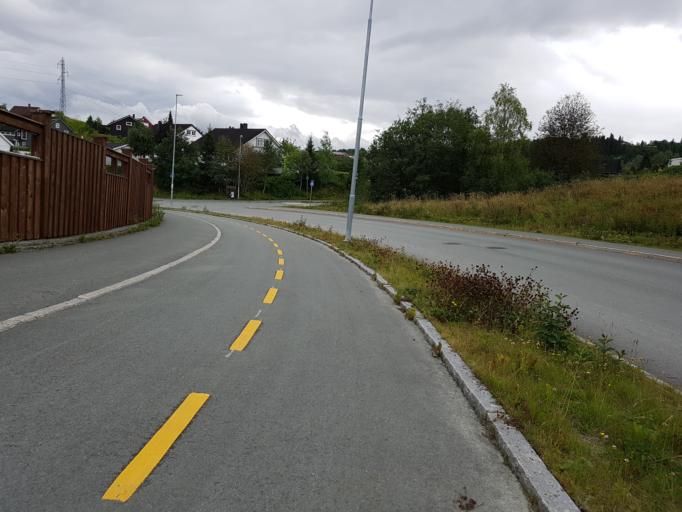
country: NO
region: Sor-Trondelag
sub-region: Trondheim
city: Trondheim
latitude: 63.3875
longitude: 10.3473
